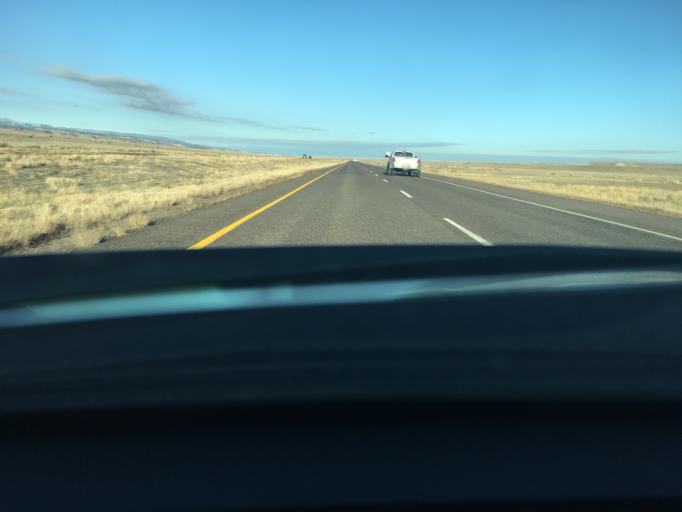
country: US
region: Colorado
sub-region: Delta County
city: Delta
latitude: 38.7893
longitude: -108.2530
